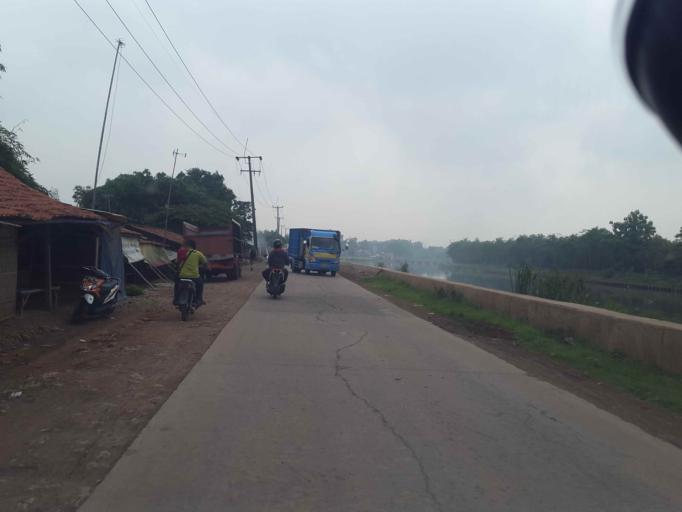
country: ID
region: West Java
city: Cikarang
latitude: -6.3464
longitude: 107.2330
